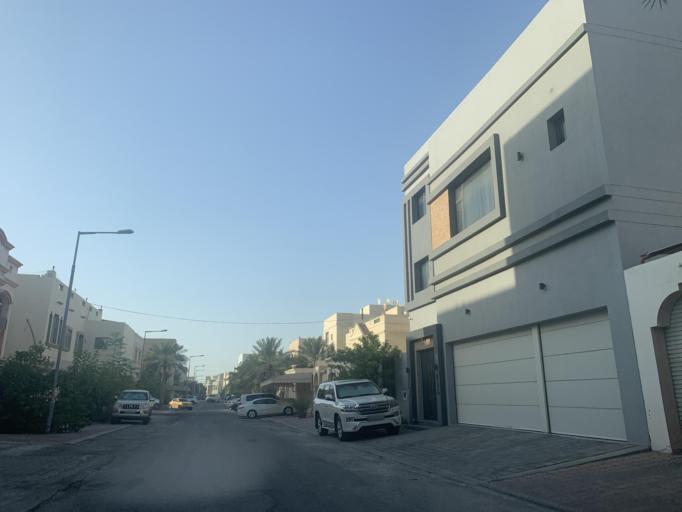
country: BH
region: Manama
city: Jidd Hafs
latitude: 26.2110
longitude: 50.5273
